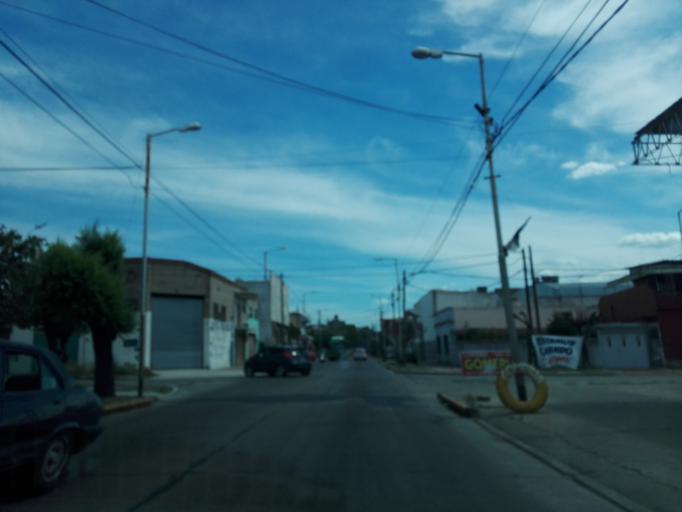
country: AR
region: Buenos Aires
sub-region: Partido de Avellaneda
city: Avellaneda
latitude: -34.6942
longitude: -58.3578
